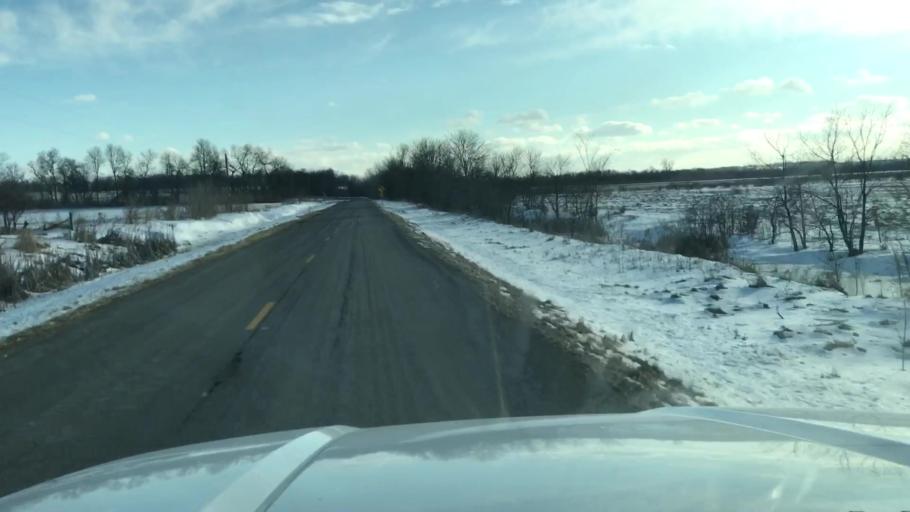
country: US
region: Missouri
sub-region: Holt County
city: Oregon
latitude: 40.1067
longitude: -95.0227
